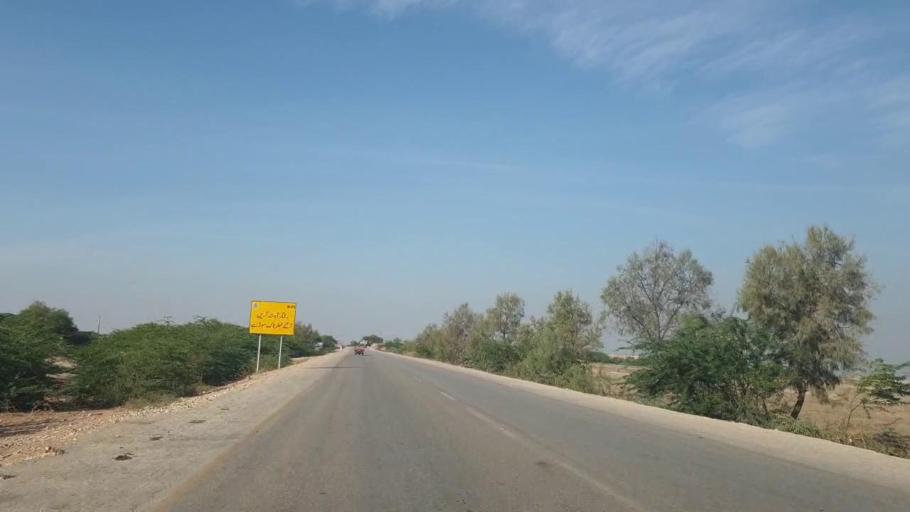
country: PK
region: Sindh
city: Sehwan
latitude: 26.3825
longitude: 67.8716
